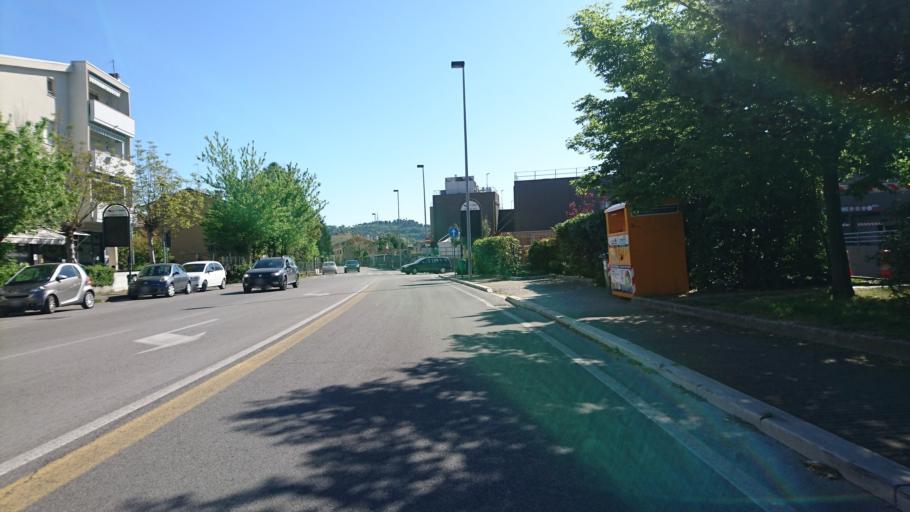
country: IT
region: The Marches
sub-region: Provincia di Pesaro e Urbino
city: Pesaro
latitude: 43.9011
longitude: 12.9026
